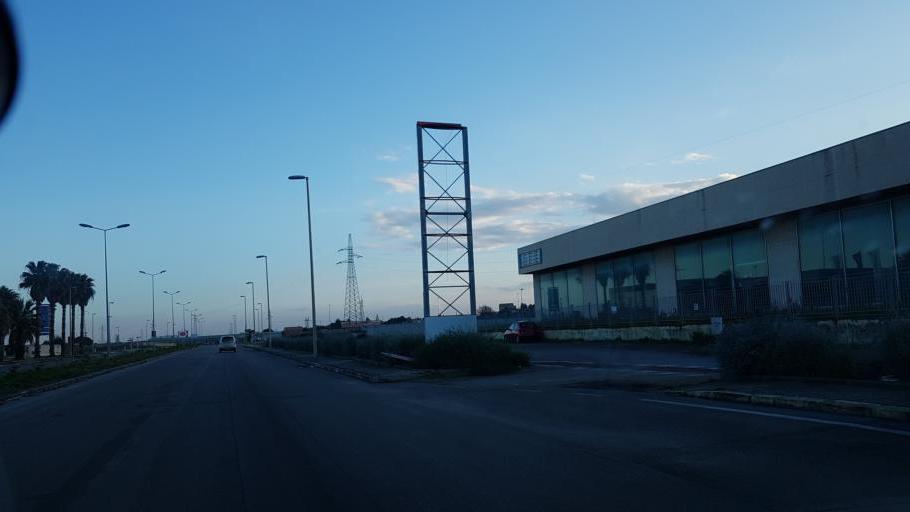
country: IT
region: Apulia
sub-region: Provincia di Lecce
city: Giorgilorio
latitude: 40.3732
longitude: 18.1370
